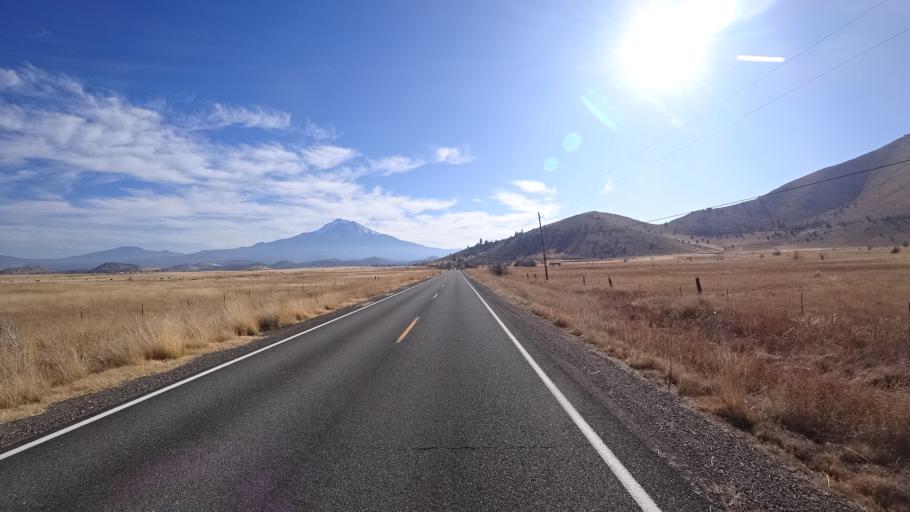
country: US
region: California
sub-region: Siskiyou County
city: Weed
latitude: 41.4724
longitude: -122.4795
